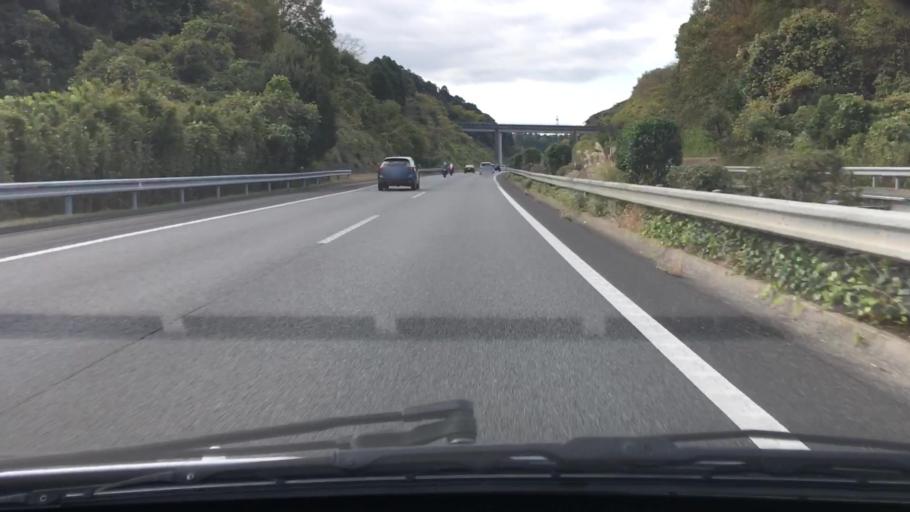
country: JP
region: Chiba
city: Ichihara
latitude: 35.4512
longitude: 140.0800
